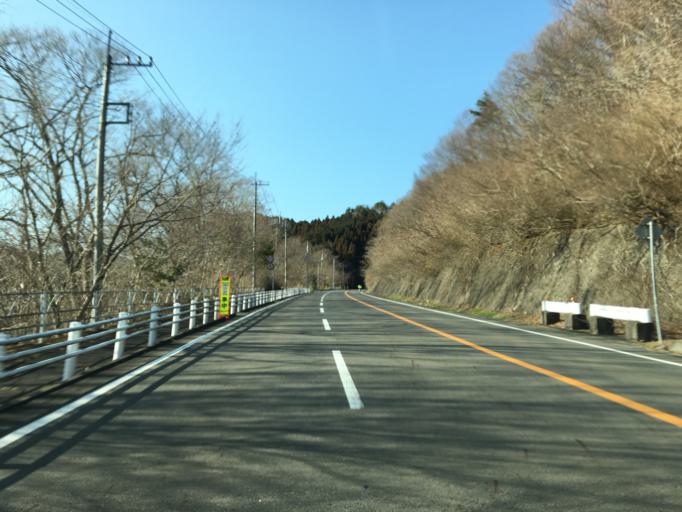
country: JP
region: Ibaraki
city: Takahagi
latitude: 36.7307
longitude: 140.6229
